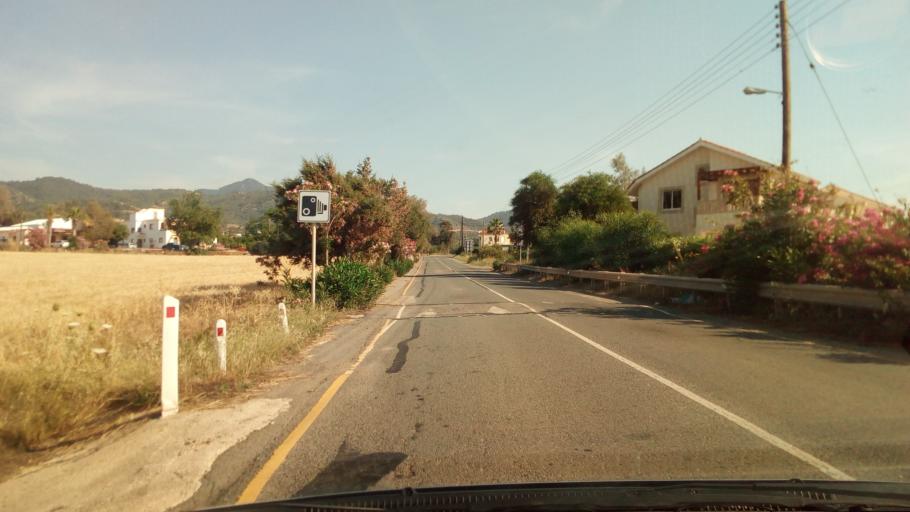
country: CY
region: Pafos
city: Polis
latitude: 35.1260
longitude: 32.5157
